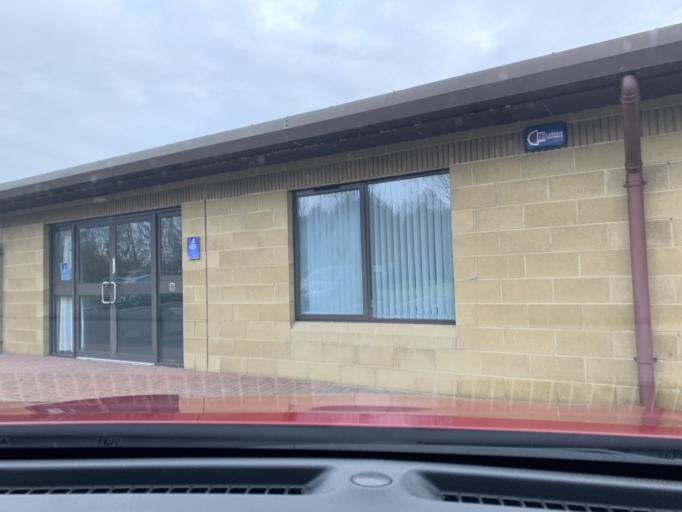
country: IE
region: Connaught
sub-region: Sligo
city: Strandhill
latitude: 54.2772
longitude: -8.5982
